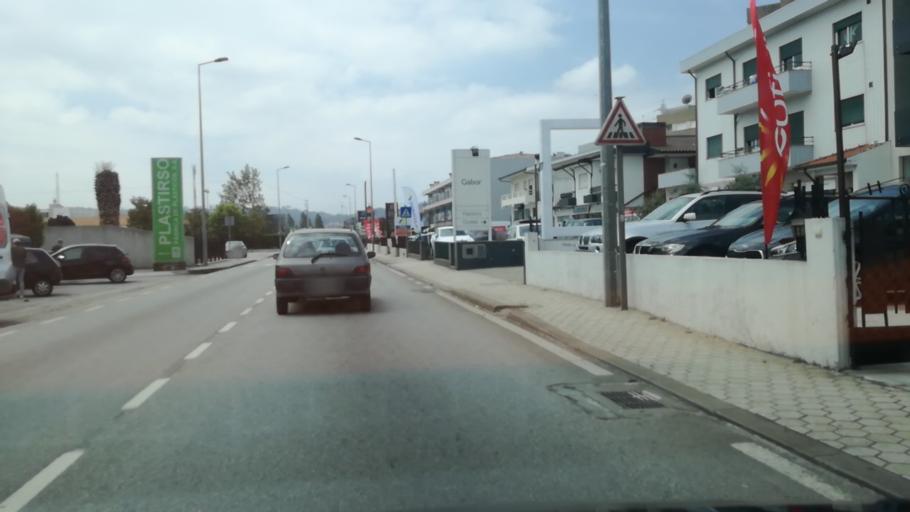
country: PT
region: Porto
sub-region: Trofa
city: Bougado
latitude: 41.3307
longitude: -8.5647
